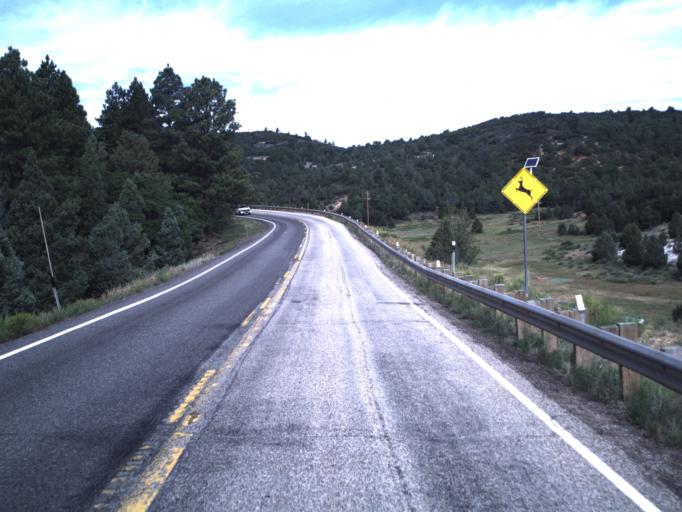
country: US
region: Utah
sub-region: Garfield County
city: Panguitch
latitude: 37.4906
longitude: -112.5207
